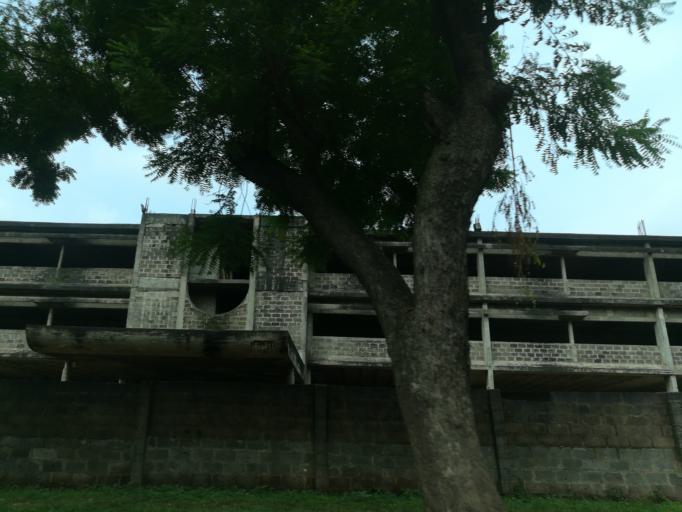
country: NG
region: Lagos
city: Ojota
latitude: 6.6098
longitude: 3.3680
